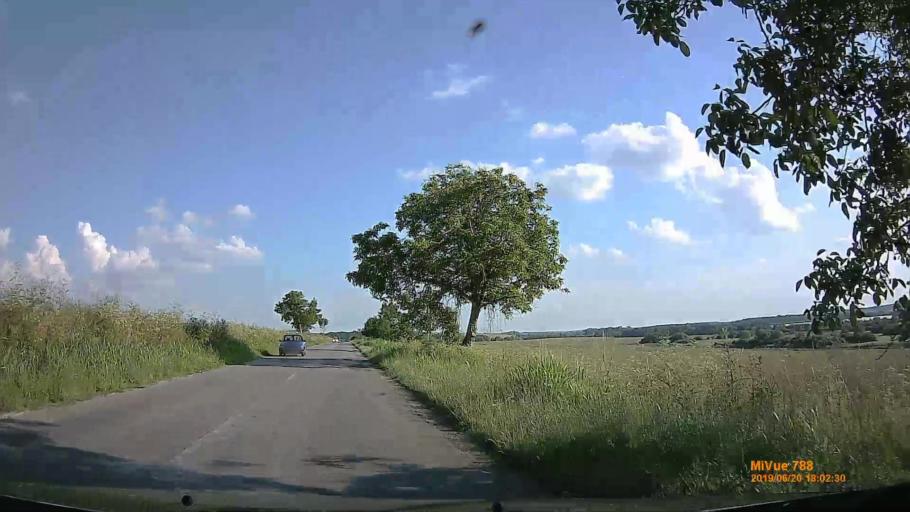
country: HU
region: Baranya
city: Buekkoesd
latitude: 46.0738
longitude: 17.9907
